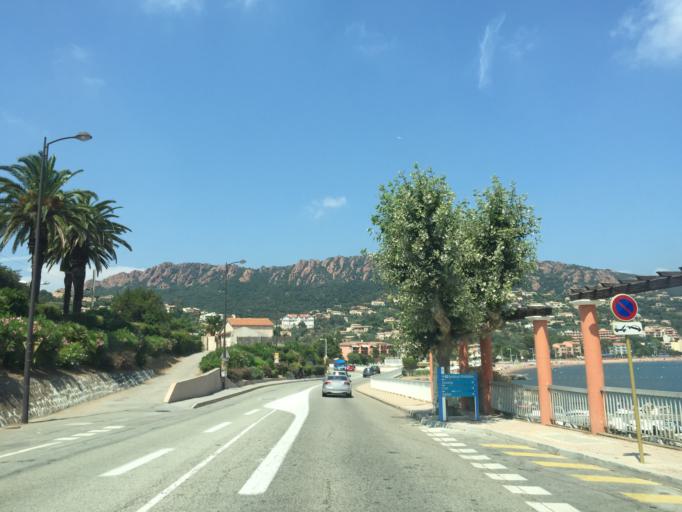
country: FR
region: Provence-Alpes-Cote d'Azur
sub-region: Departement du Var
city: Saint-Raphael
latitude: 43.4305
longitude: 6.8566
